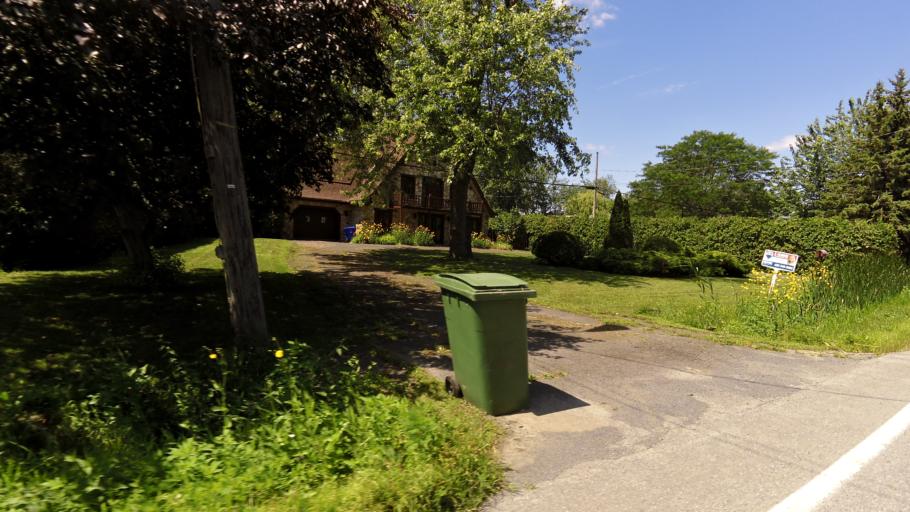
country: CA
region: Quebec
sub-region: Monteregie
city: Richelieu
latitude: 45.3973
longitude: -73.2513
